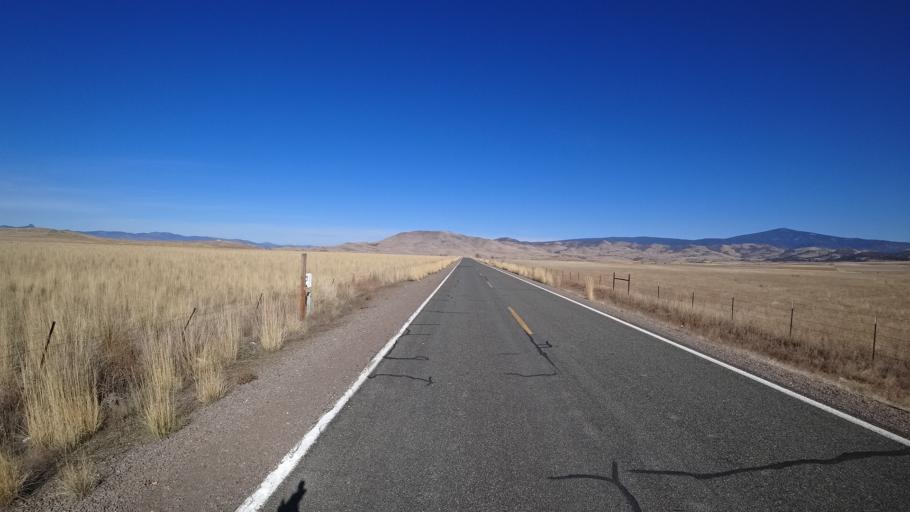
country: US
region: California
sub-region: Siskiyou County
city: Montague
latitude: 41.8012
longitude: -122.4479
